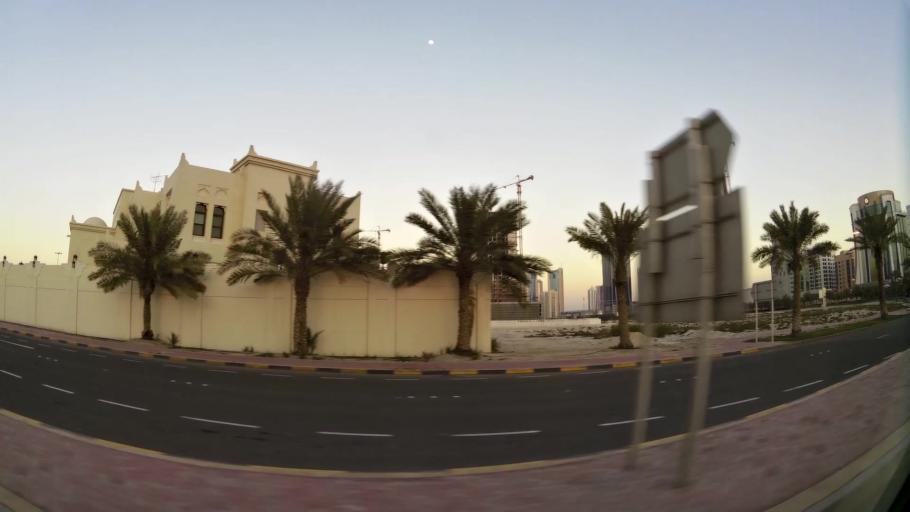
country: BH
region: Manama
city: Jidd Hafs
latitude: 26.2335
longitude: 50.5437
